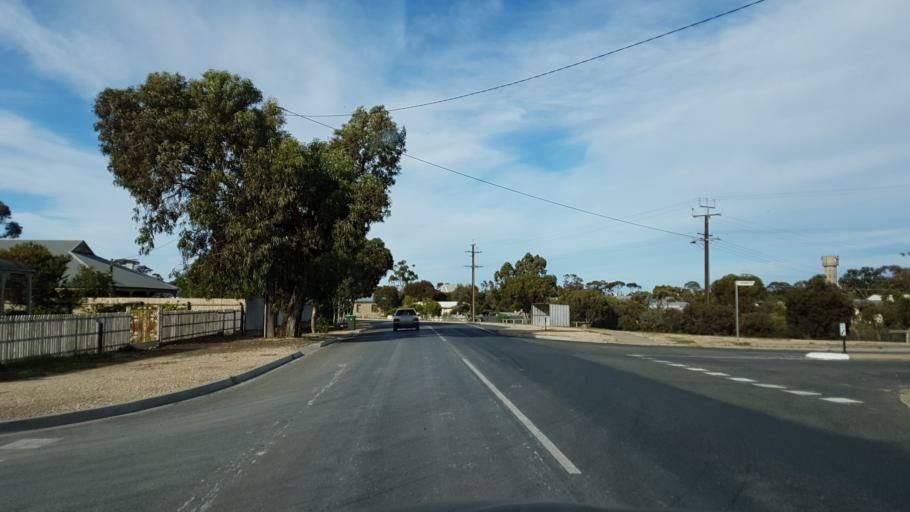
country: AU
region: South Australia
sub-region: Murray Bridge
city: Tailem Bend
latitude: -35.2495
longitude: 139.4551
